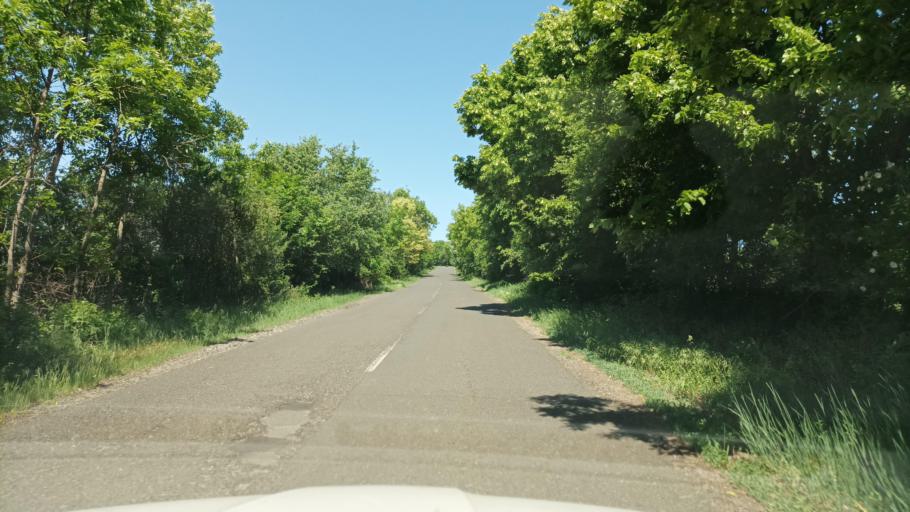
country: HU
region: Pest
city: Acsa
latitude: 47.7872
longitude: 19.4170
